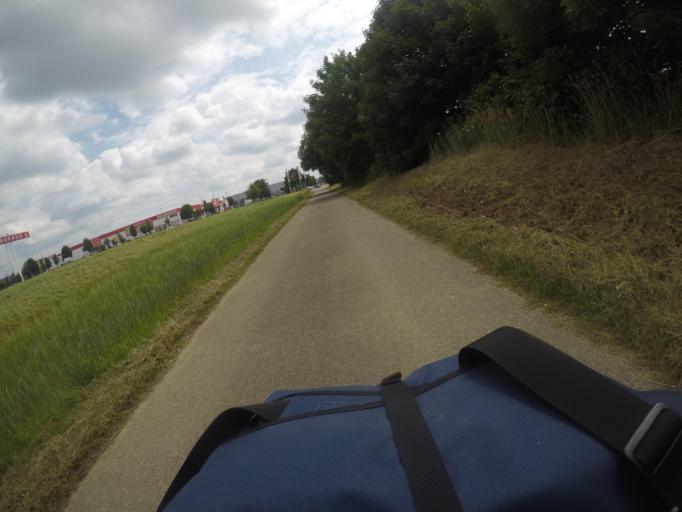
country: DE
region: Bavaria
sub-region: Swabia
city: Memmingen
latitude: 48.0046
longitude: 10.1696
